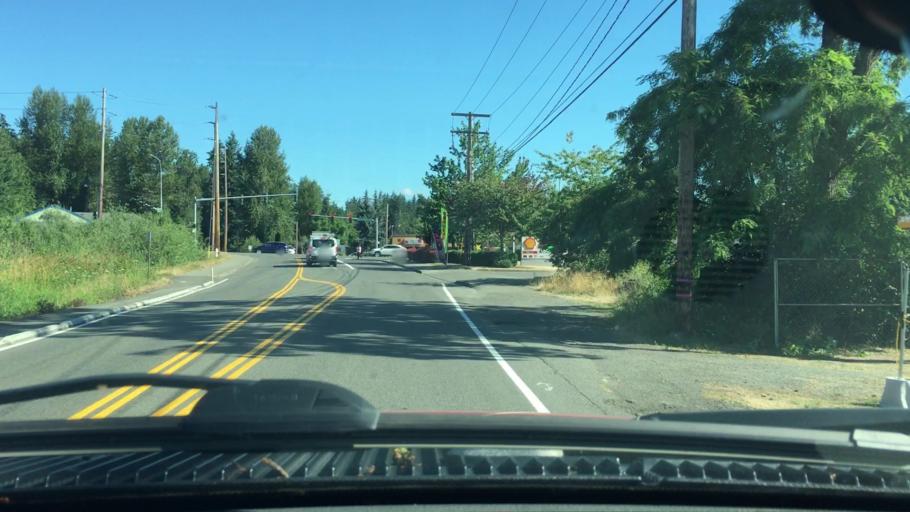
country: US
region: Washington
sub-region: King County
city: Covington
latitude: 47.3571
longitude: -122.1389
